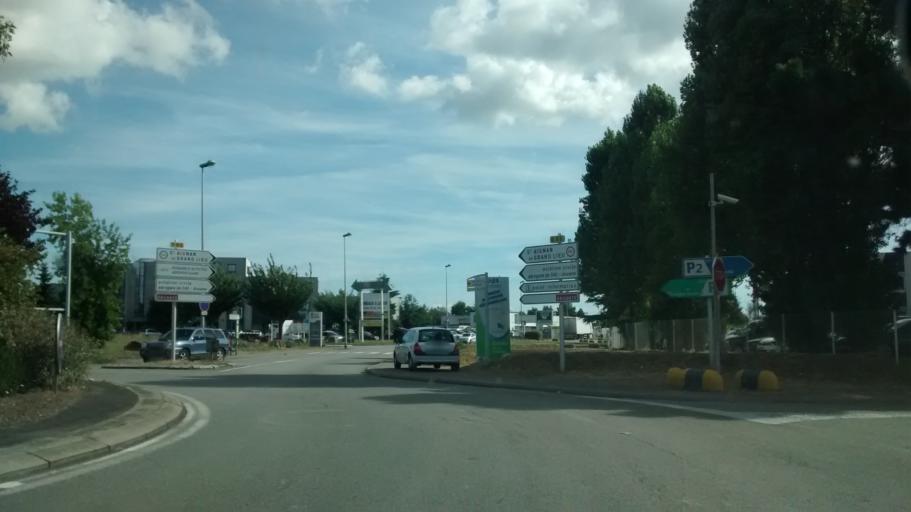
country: FR
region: Pays de la Loire
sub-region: Departement de la Loire-Atlantique
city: Bouguenais
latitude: 47.1579
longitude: -1.5973
